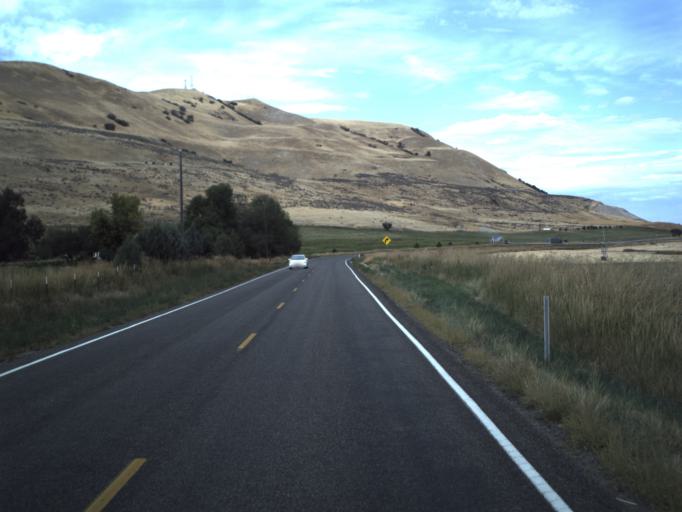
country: US
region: Utah
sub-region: Cache County
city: Benson
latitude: 41.8798
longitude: -111.9508
